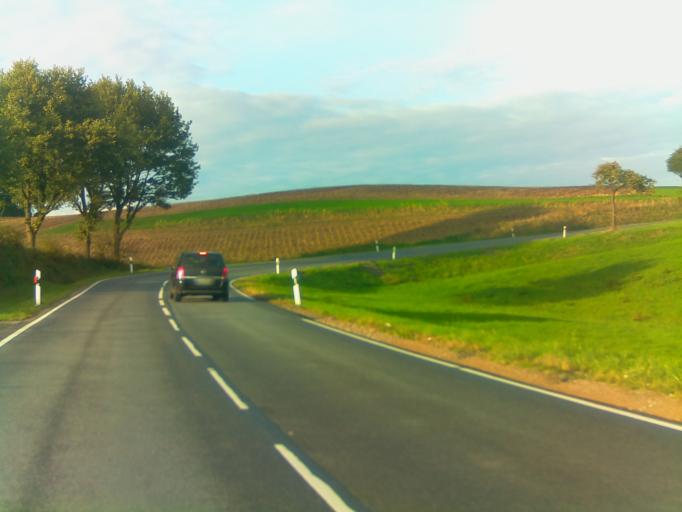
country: DE
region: Hesse
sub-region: Regierungsbezirk Darmstadt
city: Lindenfels
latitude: 49.6800
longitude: 8.8038
